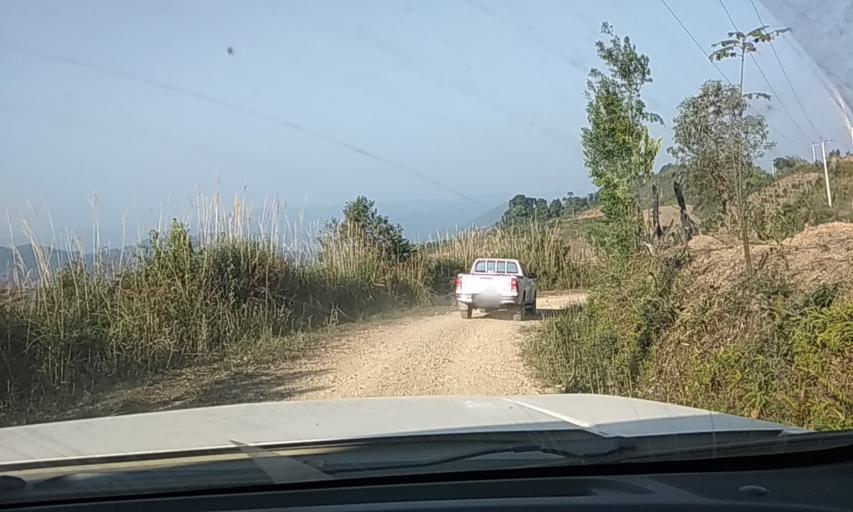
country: LA
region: Phongsali
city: Phongsali
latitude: 21.6617
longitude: 102.1756
